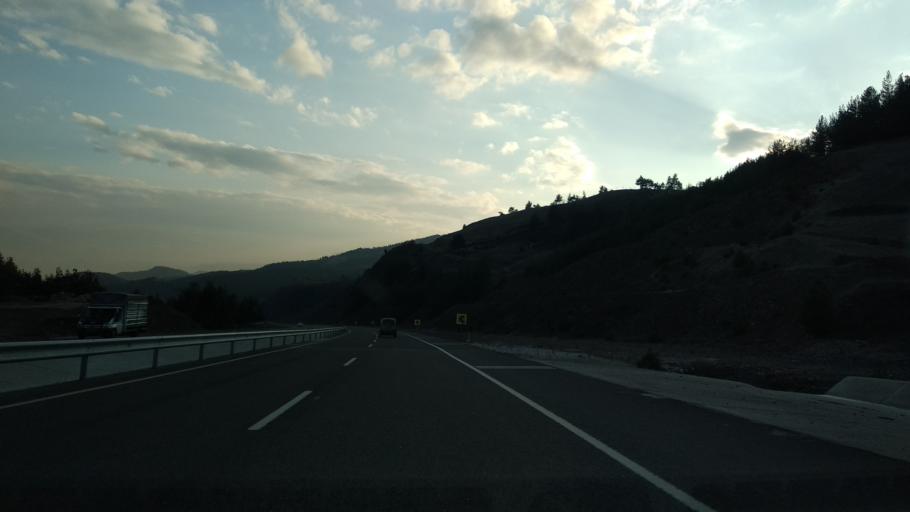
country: TR
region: Kahramanmaras
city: Yenicekale
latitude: 37.7073
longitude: 36.6894
